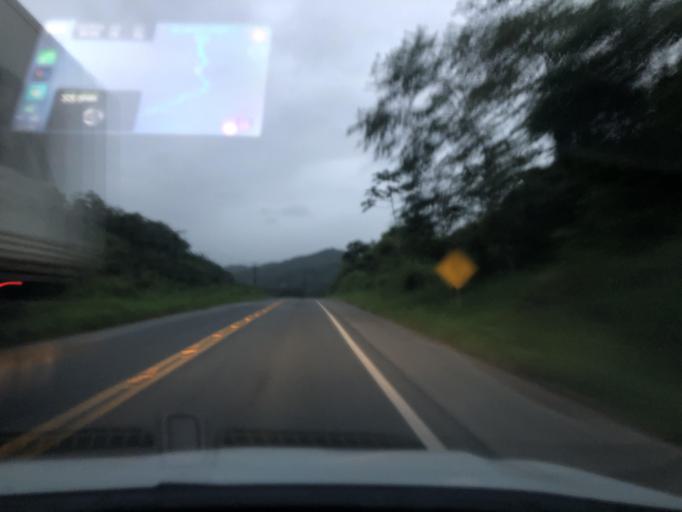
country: BR
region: Santa Catarina
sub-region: Jaragua Do Sul
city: Jaragua do Sul
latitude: -26.6530
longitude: -49.0257
